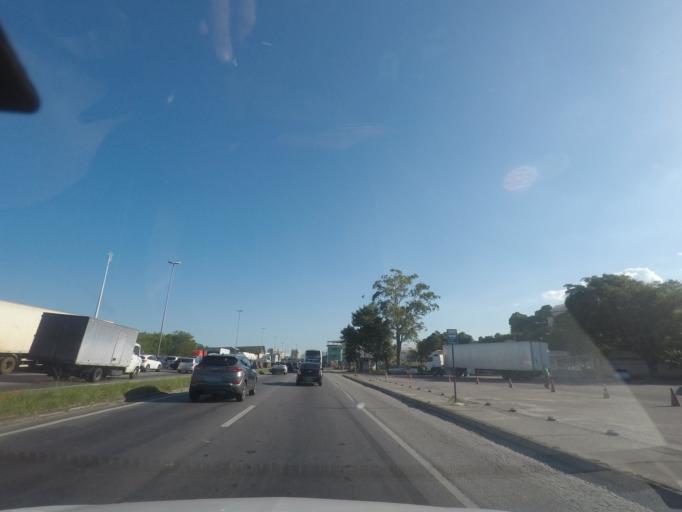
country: BR
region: Rio de Janeiro
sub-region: Duque De Caxias
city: Duque de Caxias
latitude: -22.7798
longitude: -43.2860
